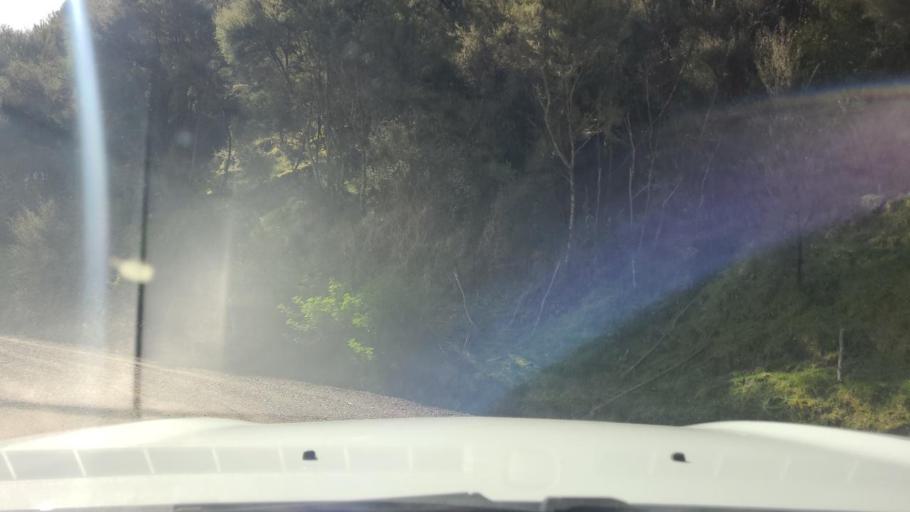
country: NZ
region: Wellington
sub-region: South Wairarapa District
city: Waipawa
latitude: -41.3489
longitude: 175.6760
